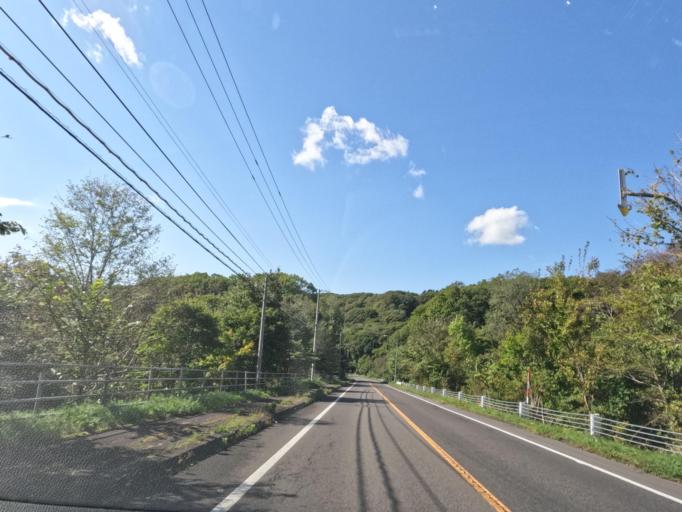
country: JP
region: Hokkaido
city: Muroran
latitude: 42.4415
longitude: 141.1124
